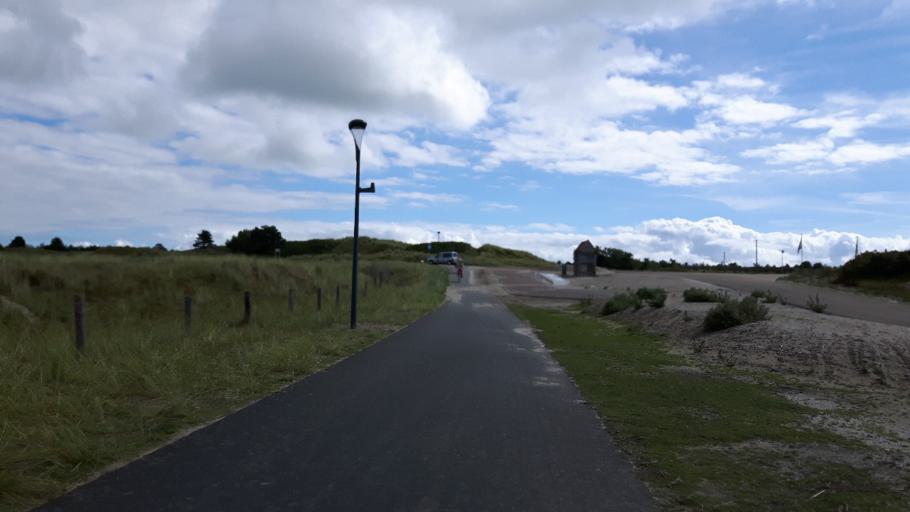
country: NL
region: Friesland
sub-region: Gemeente Ameland
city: Hollum
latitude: 53.4491
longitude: 5.6199
